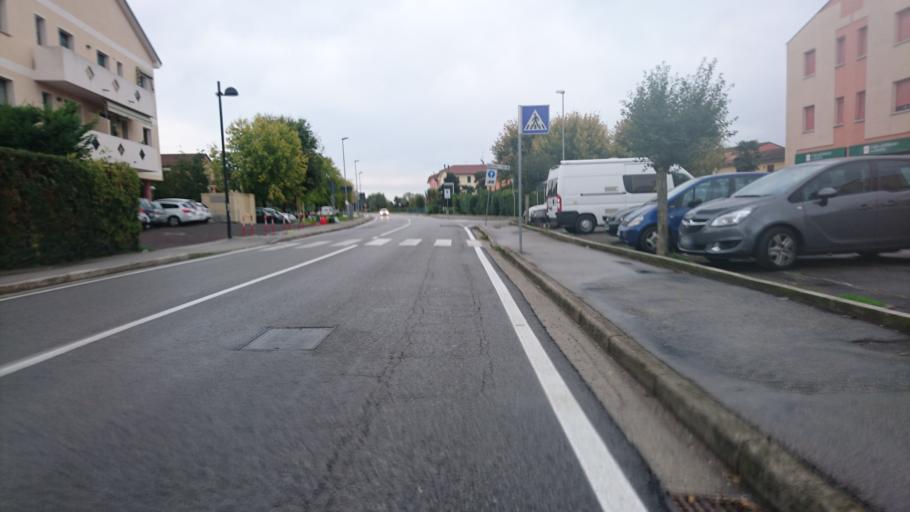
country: IT
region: Veneto
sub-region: Provincia di Padova
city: Veggiano
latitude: 45.4462
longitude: 11.7161
